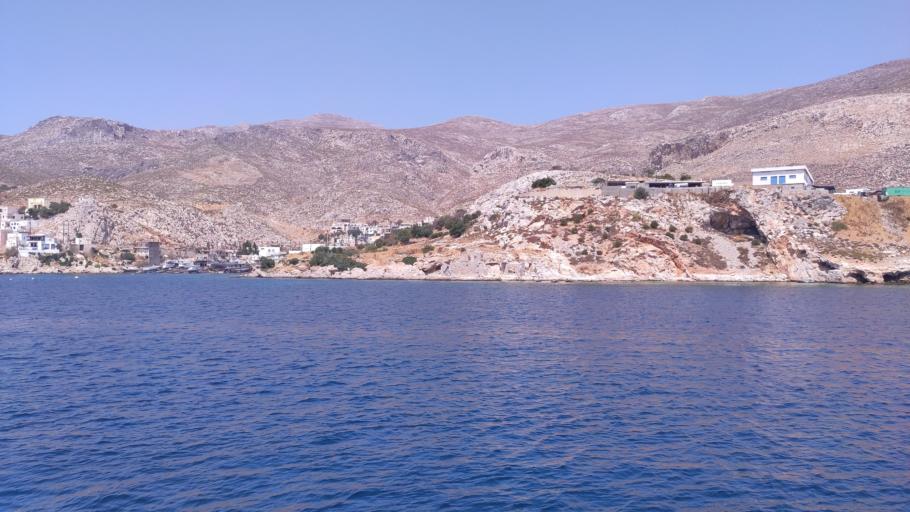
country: GR
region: South Aegean
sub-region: Nomos Dodekanisou
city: Kalymnos
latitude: 36.9481
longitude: 26.9970
